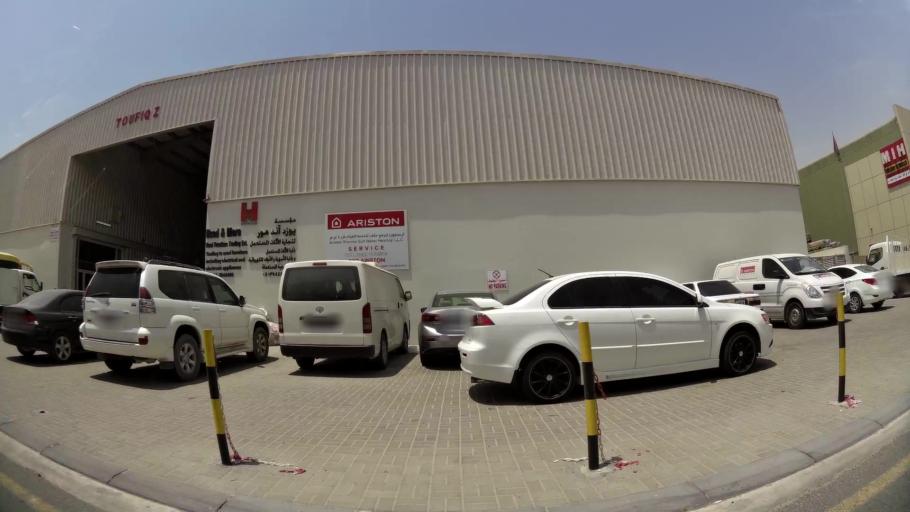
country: AE
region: Ash Shariqah
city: Sharjah
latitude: 25.1855
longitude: 55.3804
